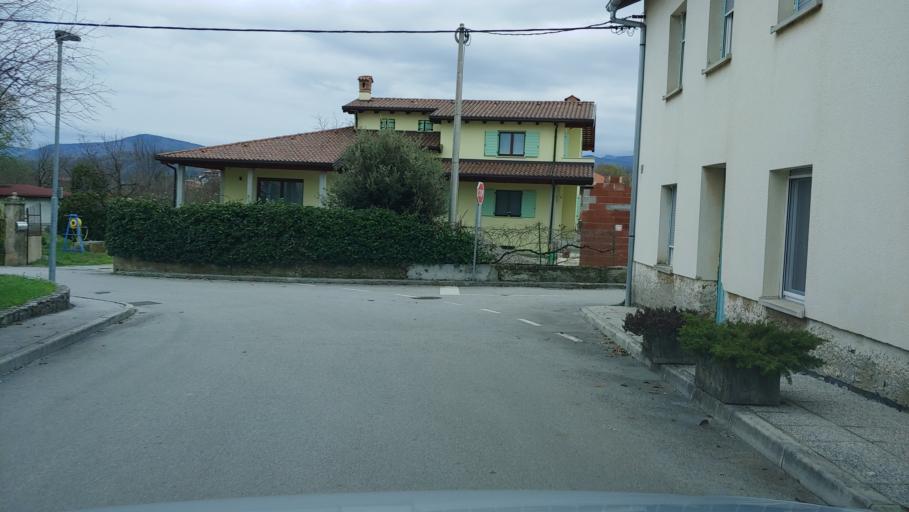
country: SI
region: Sempeter-Vrtojba
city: Vrtojba
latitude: 45.9082
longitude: 13.6365
